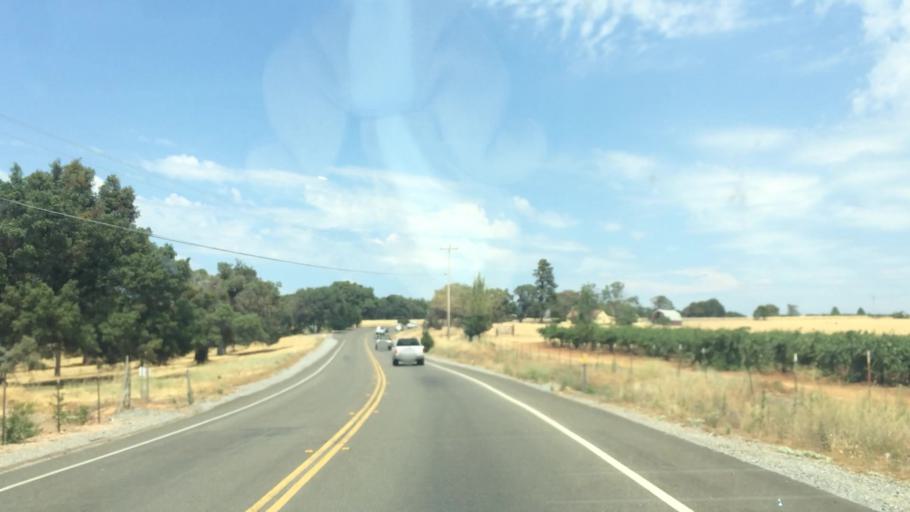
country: US
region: California
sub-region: Amador County
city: Sutter Creek
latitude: 38.3990
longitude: -120.7544
